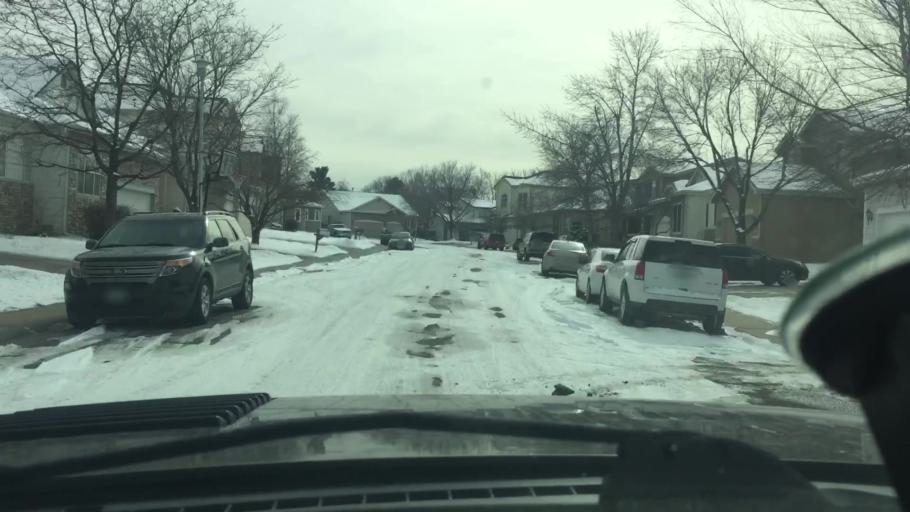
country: US
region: Colorado
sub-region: Adams County
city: Northglenn
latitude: 39.8987
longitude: -105.0046
